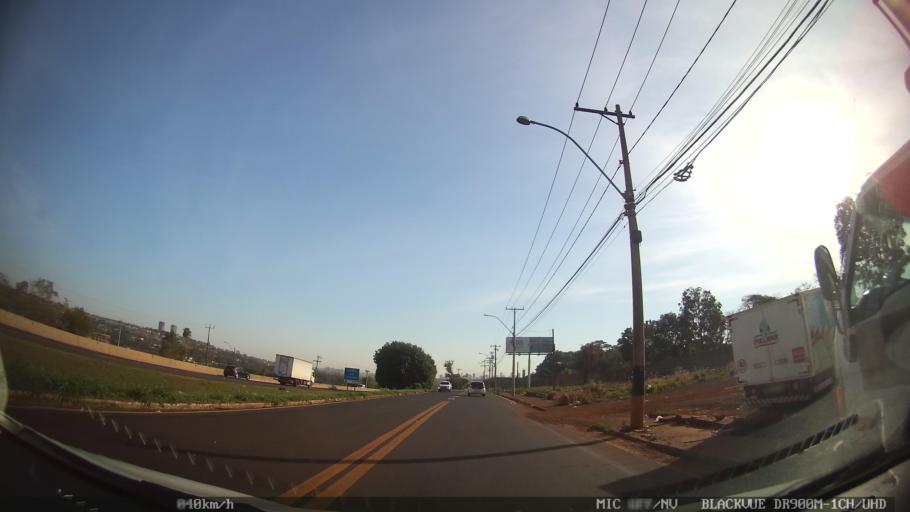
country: BR
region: Sao Paulo
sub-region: Ribeirao Preto
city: Ribeirao Preto
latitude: -21.2546
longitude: -47.8188
